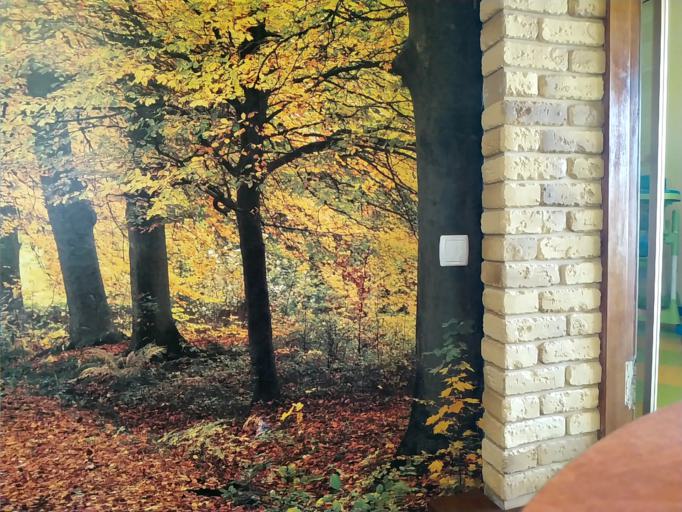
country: RU
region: Tverskaya
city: Rameshki
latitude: 57.5420
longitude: 35.9532
